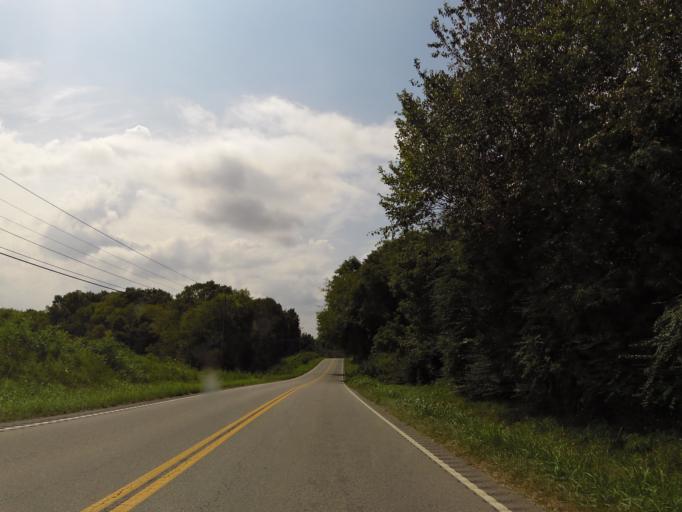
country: US
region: Tennessee
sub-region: Perry County
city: Linden
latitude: 35.6842
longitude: -87.8044
